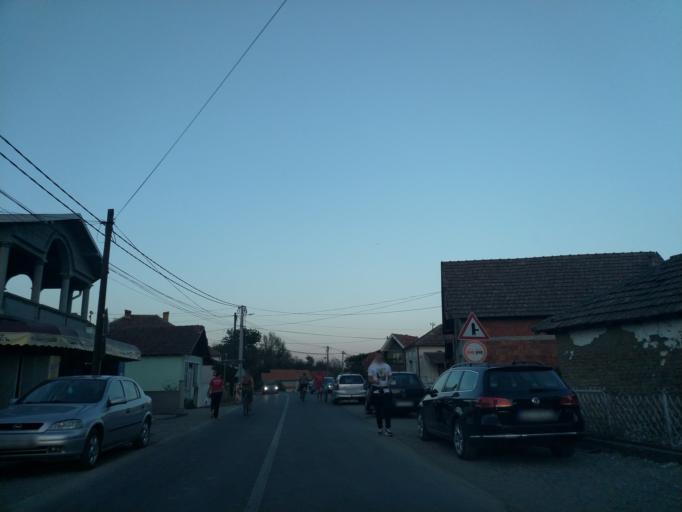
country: RS
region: Central Serbia
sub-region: Rasinski Okrug
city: Krusevac
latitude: 43.6155
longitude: 21.2986
